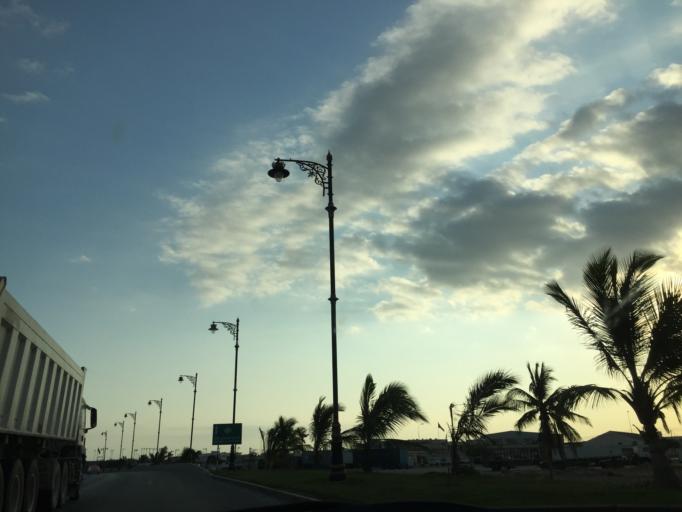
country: OM
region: Zufar
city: Salalah
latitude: 17.0227
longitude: 54.0575
